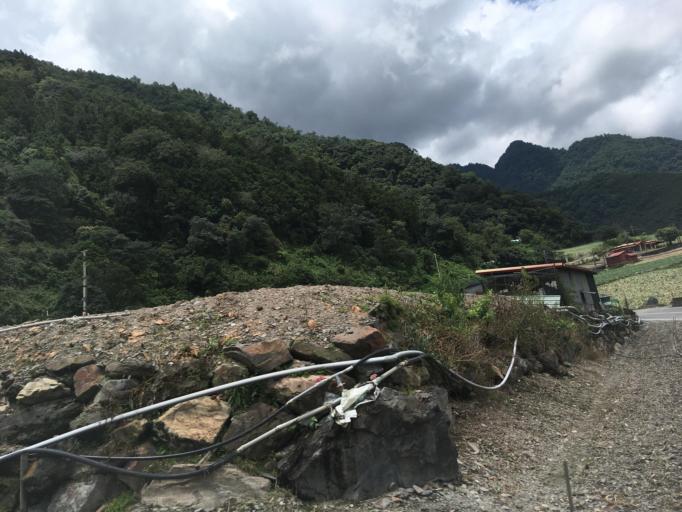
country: TW
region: Taiwan
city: Daxi
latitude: 24.4575
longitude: 121.3942
